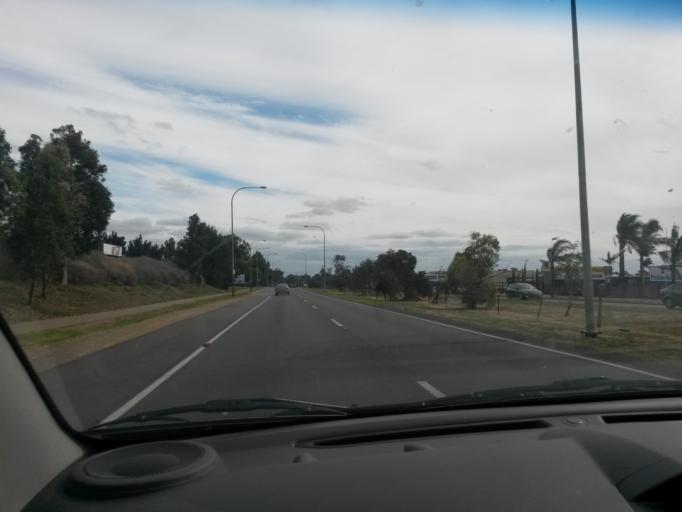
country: AU
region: South Australia
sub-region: Salisbury
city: Salisbury
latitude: -34.7697
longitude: 138.6665
